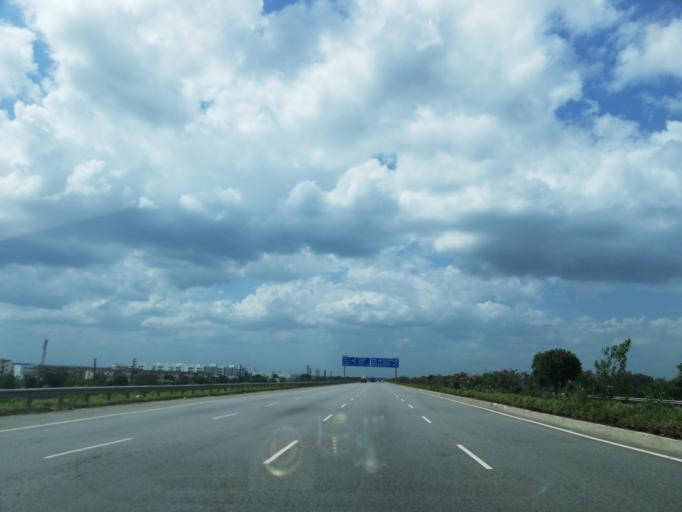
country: IN
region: Telangana
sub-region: Medak
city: Serilingampalle
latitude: 17.4415
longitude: 78.2584
